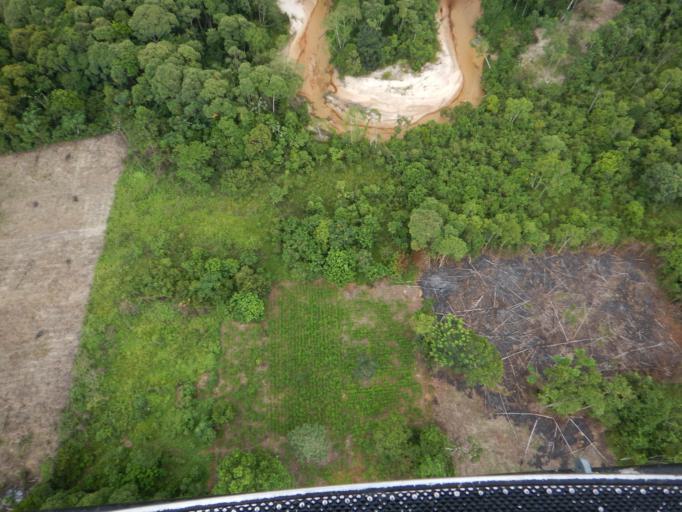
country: BO
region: Cochabamba
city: Chimore
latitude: -17.0007
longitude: -65.0505
